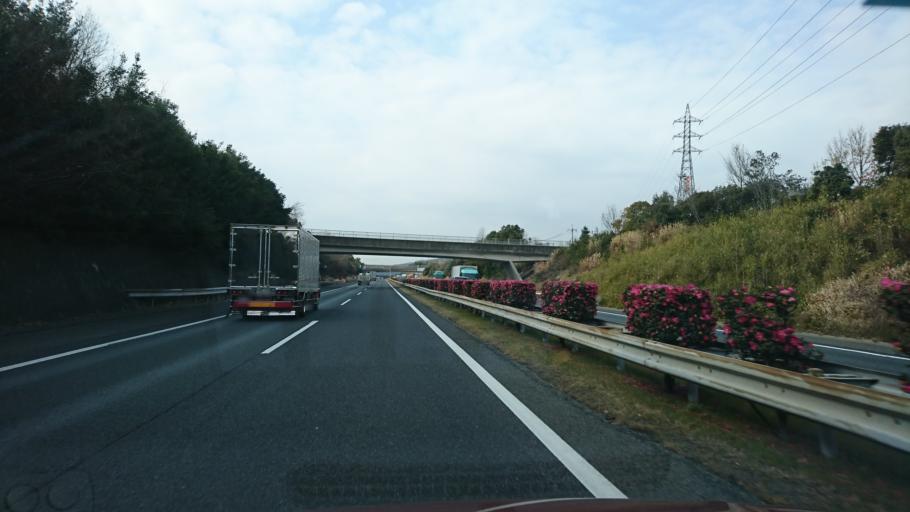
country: JP
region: Hiroshima
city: Kannabecho-yahiro
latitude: 34.5257
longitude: 133.4379
